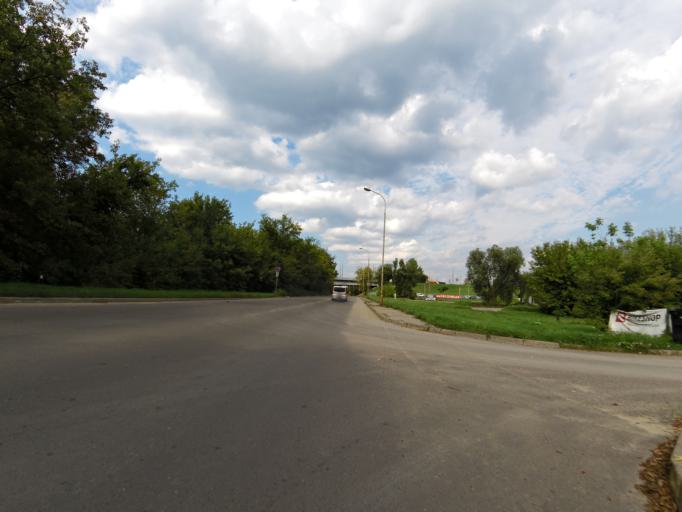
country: LT
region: Vilnius County
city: Vilkpede
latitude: 54.6681
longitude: 25.2296
